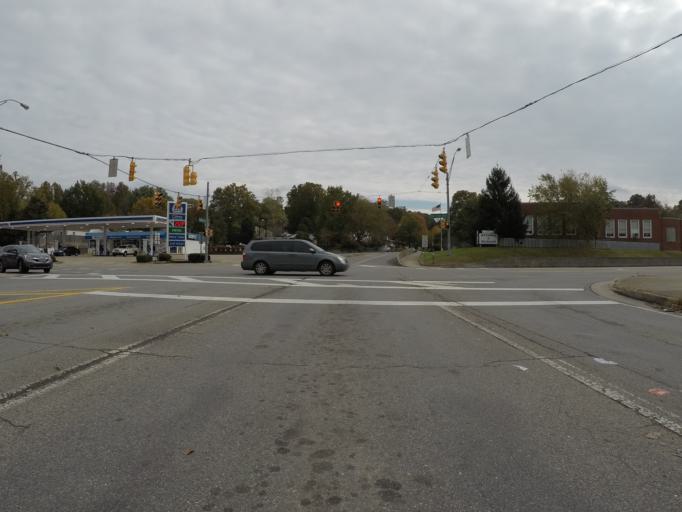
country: US
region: West Virginia
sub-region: Cabell County
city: Huntington
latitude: 38.4044
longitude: -82.4284
